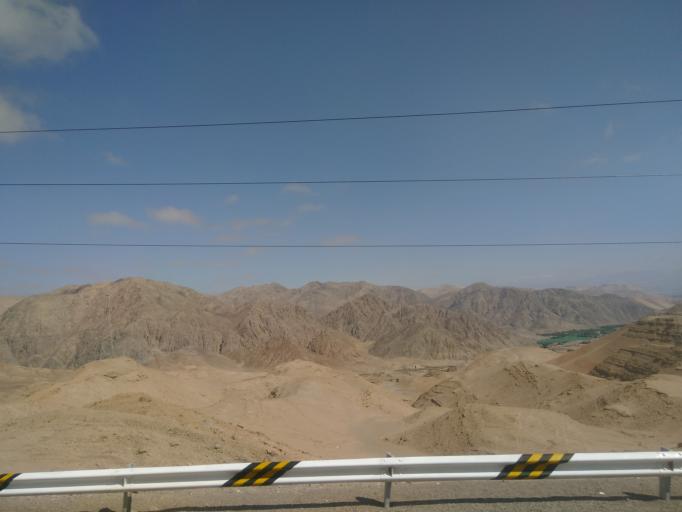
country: PE
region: Moquegua
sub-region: Provincia de Mariscal Nieto
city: Moquegua
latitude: -17.3899
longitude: -71.0130
